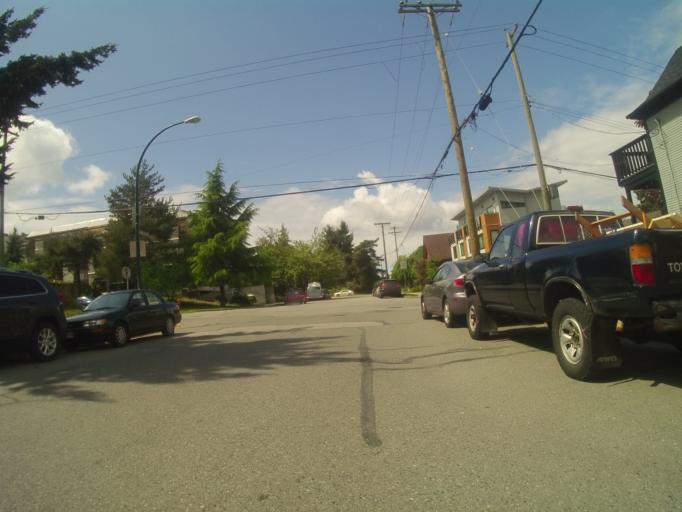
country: CA
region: British Columbia
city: Vancouver
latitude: 49.2653
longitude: -123.0945
